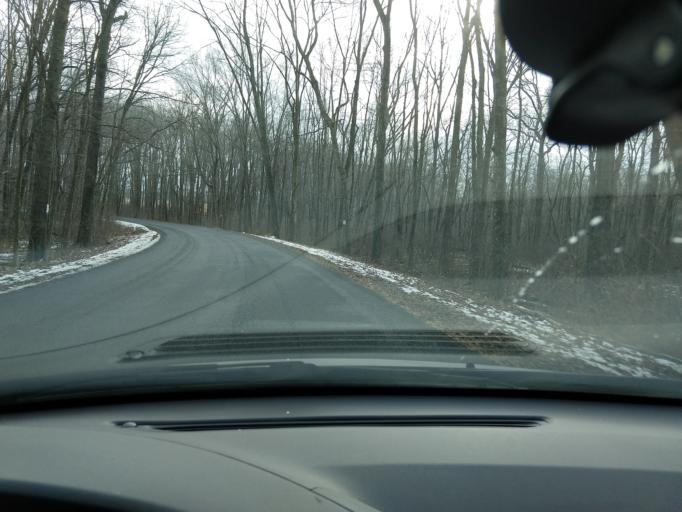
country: US
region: Pennsylvania
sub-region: Chester County
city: Elverson
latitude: 40.1938
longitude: -75.7938
